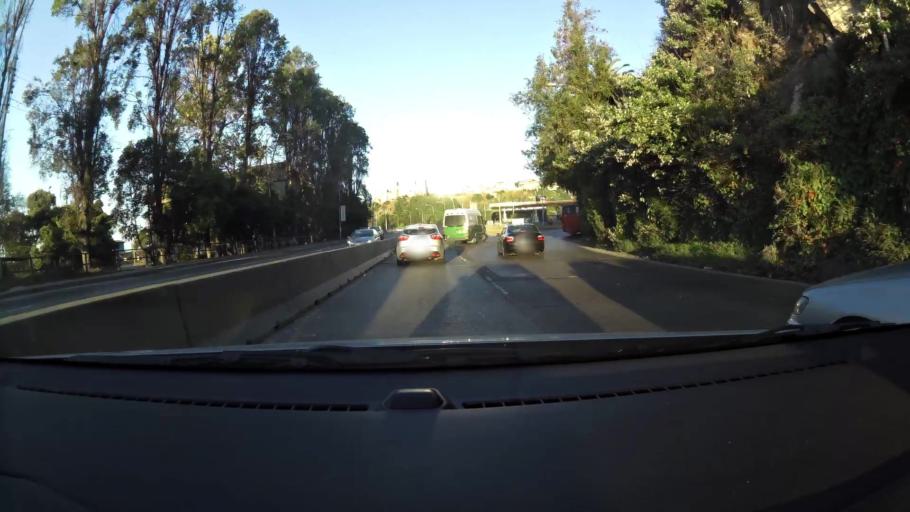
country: CL
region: Valparaiso
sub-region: Provincia de Valparaiso
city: Valparaiso
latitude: -33.0382
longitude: -71.6017
